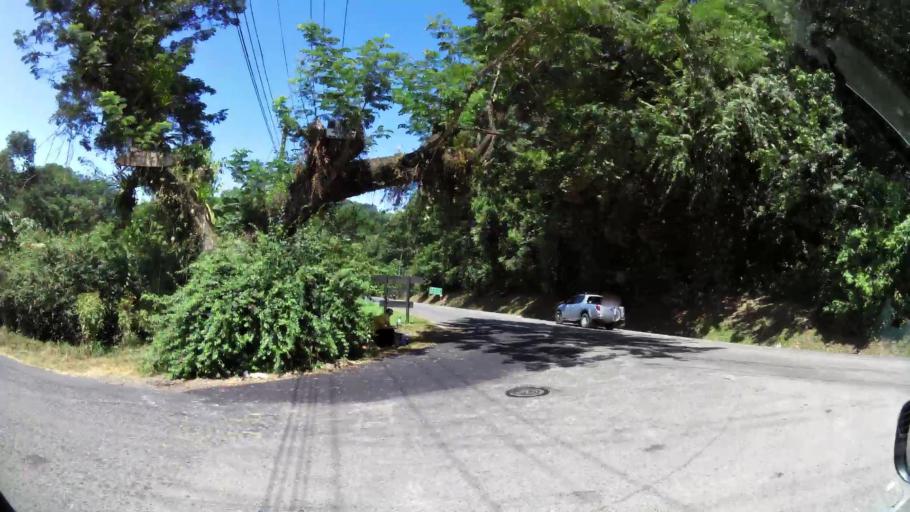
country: CR
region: San Jose
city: San Isidro
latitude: 9.2568
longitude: -83.8624
